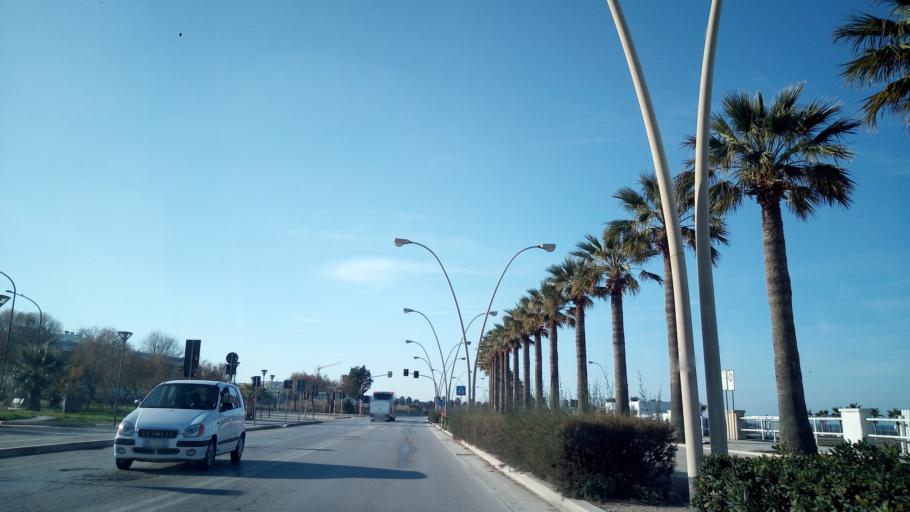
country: IT
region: Apulia
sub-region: Provincia di Barletta - Andria - Trani
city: Barletta
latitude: 41.3235
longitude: 16.2761
